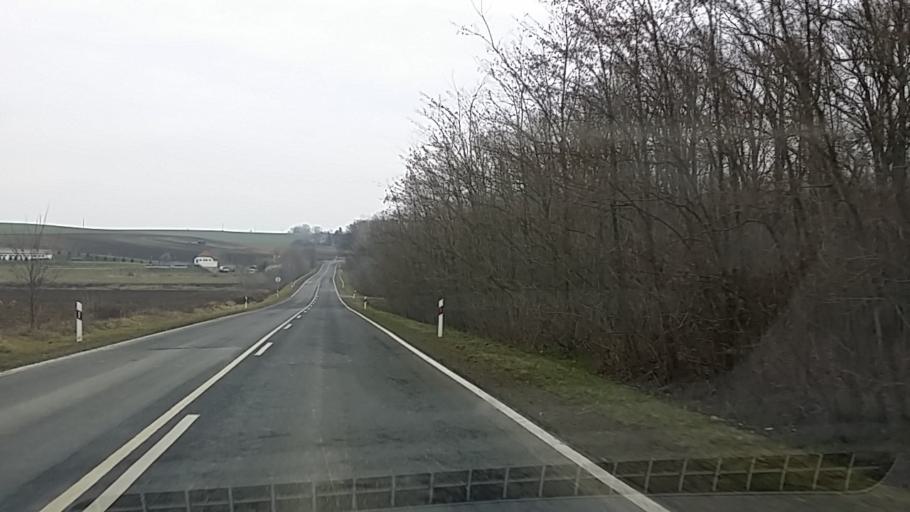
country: HU
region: Baranya
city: Dunaszekcso
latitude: 46.0630
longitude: 18.7381
